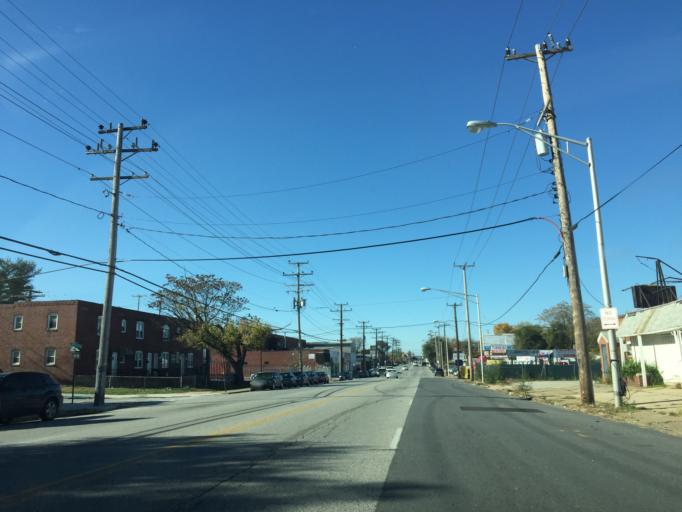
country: US
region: Maryland
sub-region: Anne Arundel County
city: Brooklyn Park
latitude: 39.2337
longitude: -76.5937
